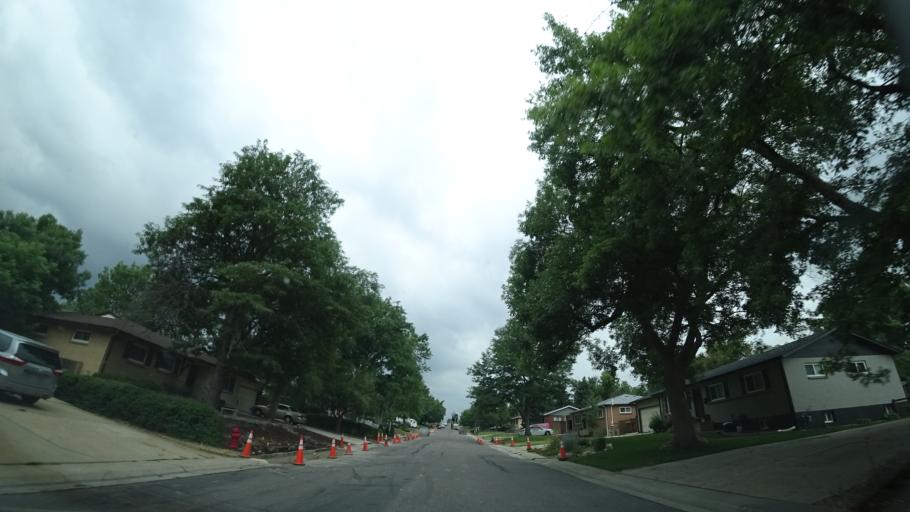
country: US
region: Colorado
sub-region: Jefferson County
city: Lakewood
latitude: 39.7040
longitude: -105.1295
